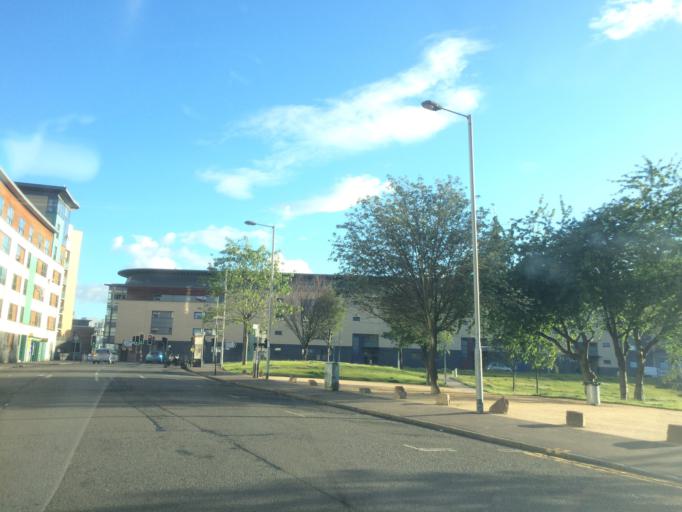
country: GB
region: Scotland
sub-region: Glasgow City
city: Glasgow
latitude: 55.8559
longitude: -4.2405
